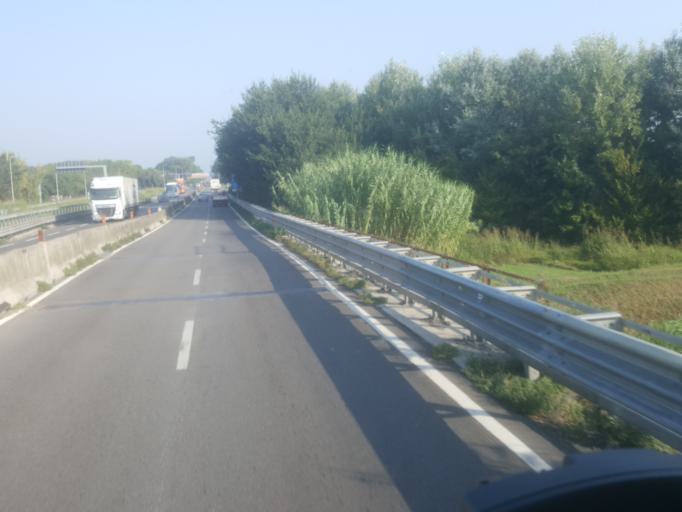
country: IT
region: Emilia-Romagna
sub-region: Provincia di Ravenna
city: Madonna Dell'Albero
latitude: 44.3959
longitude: 12.1832
